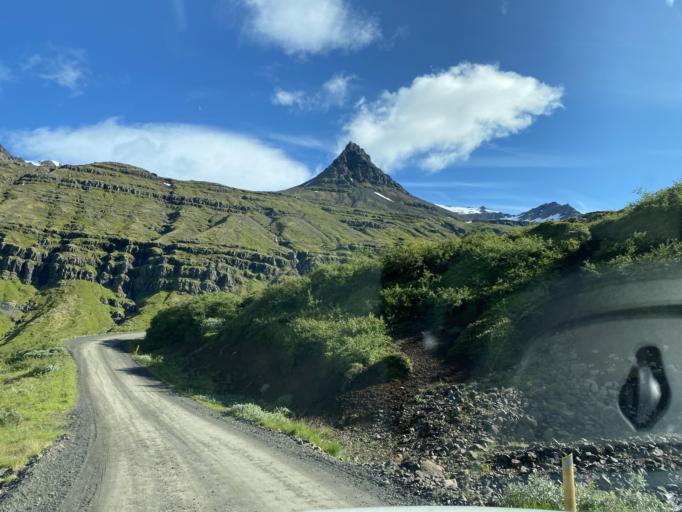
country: IS
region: East
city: Eskifjoerdur
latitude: 65.1825
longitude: -14.0755
